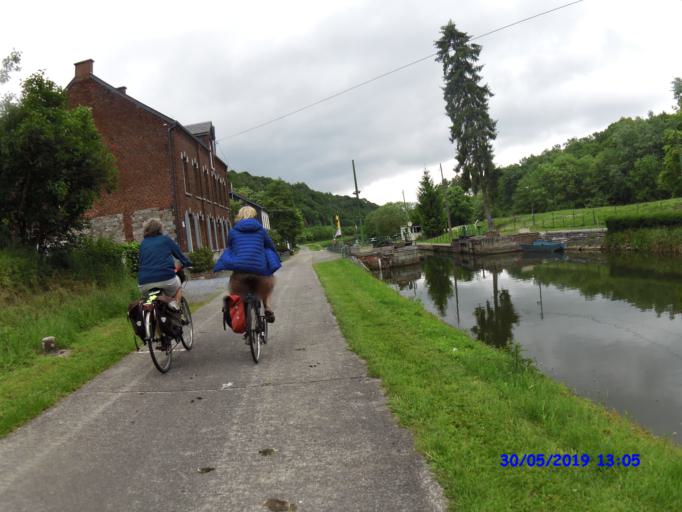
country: BE
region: Wallonia
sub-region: Province du Hainaut
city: Thuin
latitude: 50.3491
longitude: 4.3084
